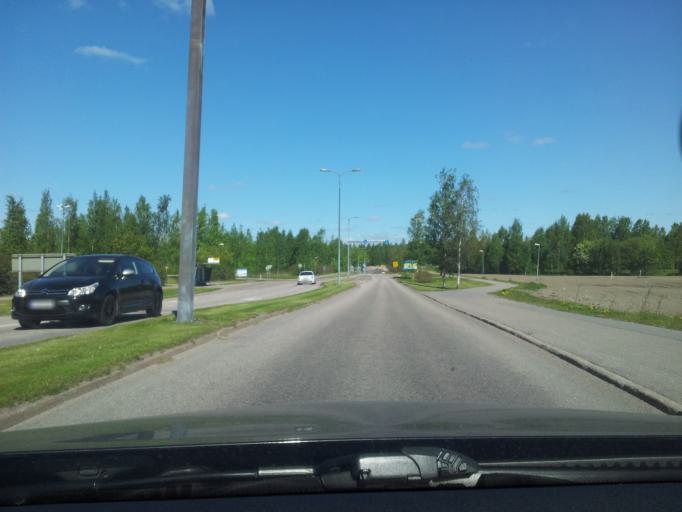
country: FI
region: Uusimaa
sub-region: Helsinki
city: Koukkuniemi
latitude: 60.1818
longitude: 24.7792
